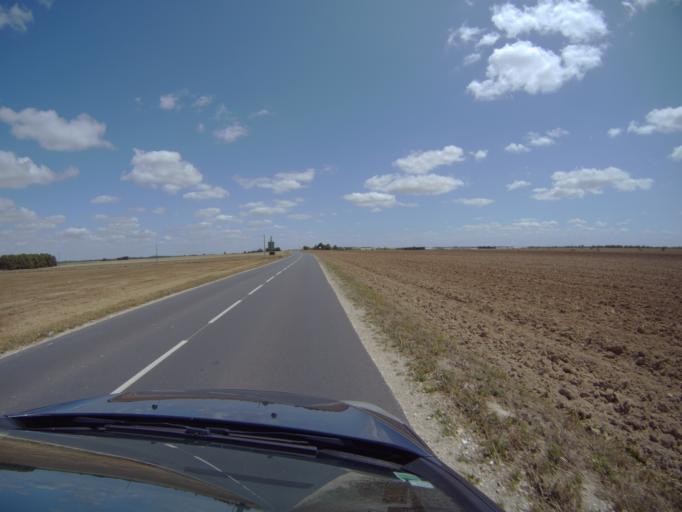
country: FR
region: Poitou-Charentes
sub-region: Departement de la Charente-Maritime
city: Marans
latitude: 46.2928
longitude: -0.9636
